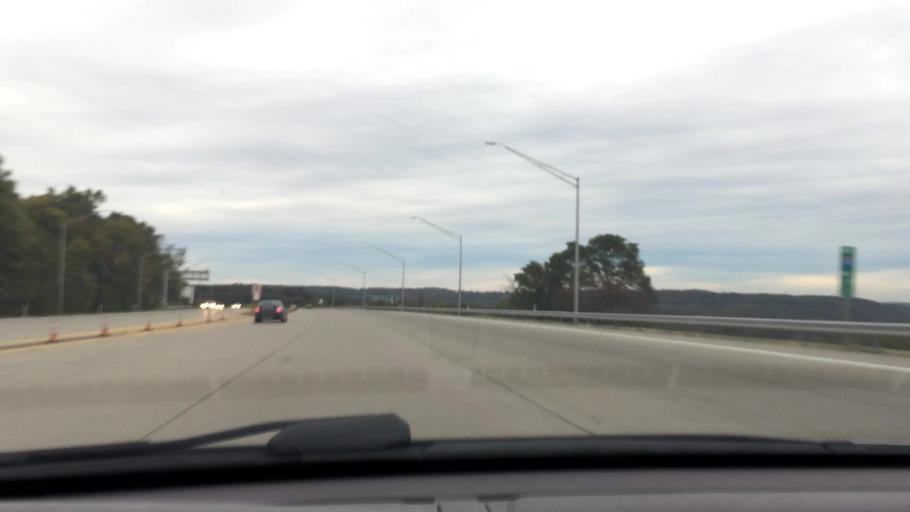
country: US
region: Pennsylvania
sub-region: Lawrence County
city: Oakland
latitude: 40.9463
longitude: -80.3915
